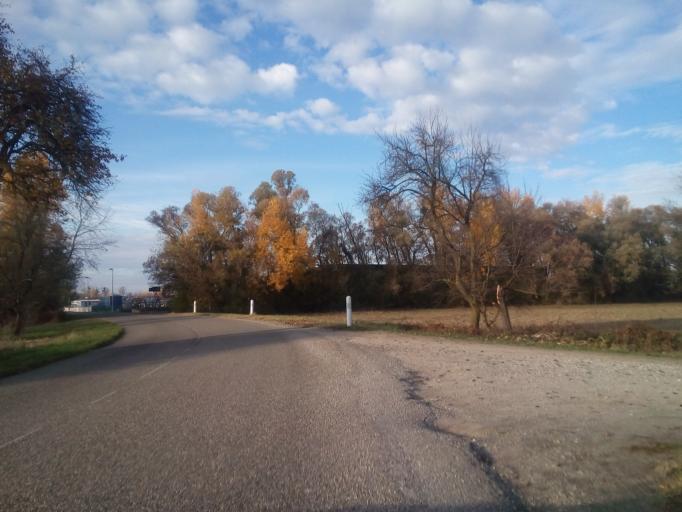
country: FR
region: Alsace
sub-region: Departement du Bas-Rhin
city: Herrlisheim
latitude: 48.7025
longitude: 7.9205
